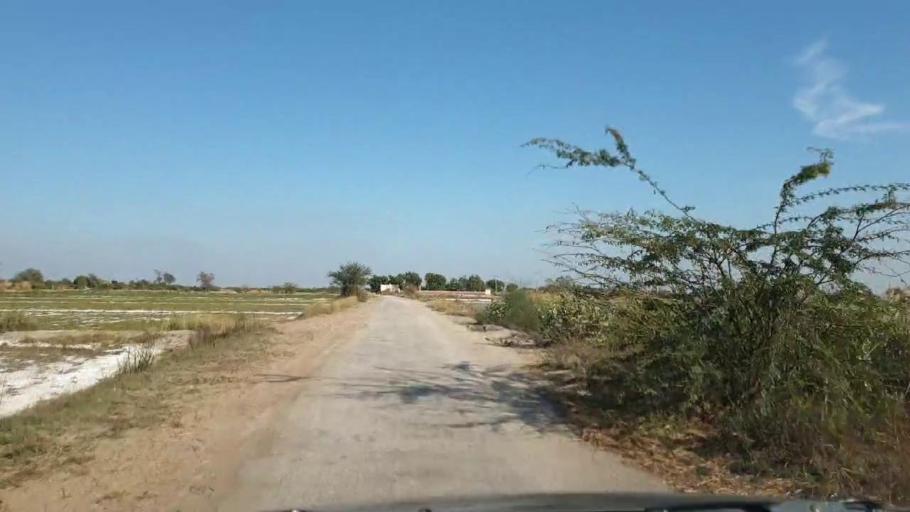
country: PK
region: Sindh
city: Khadro
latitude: 26.1899
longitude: 68.7634
